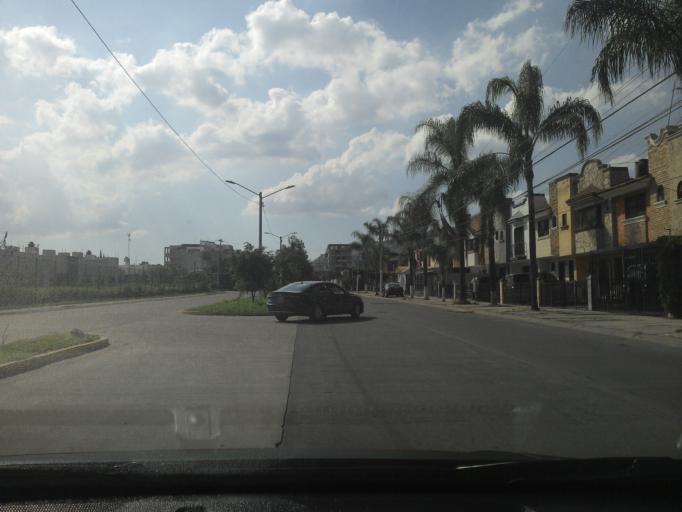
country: MX
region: Jalisco
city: Guadalajara
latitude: 20.6527
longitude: -103.4373
